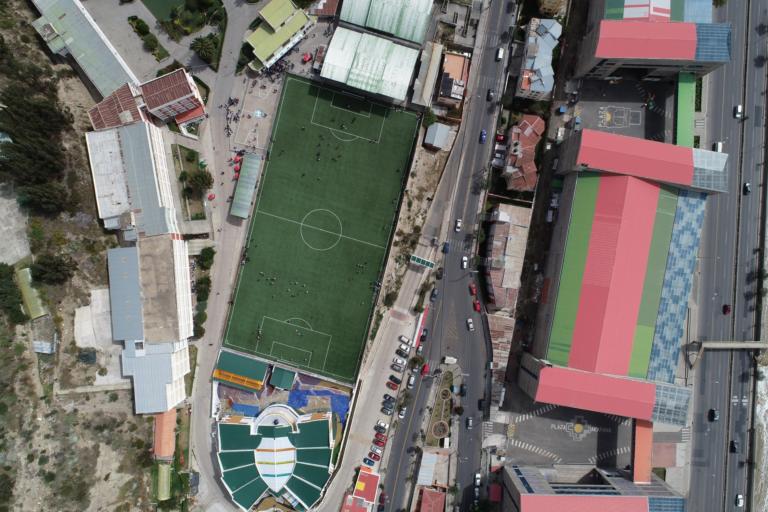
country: BO
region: La Paz
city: La Paz
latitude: -16.5371
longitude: -68.0972
